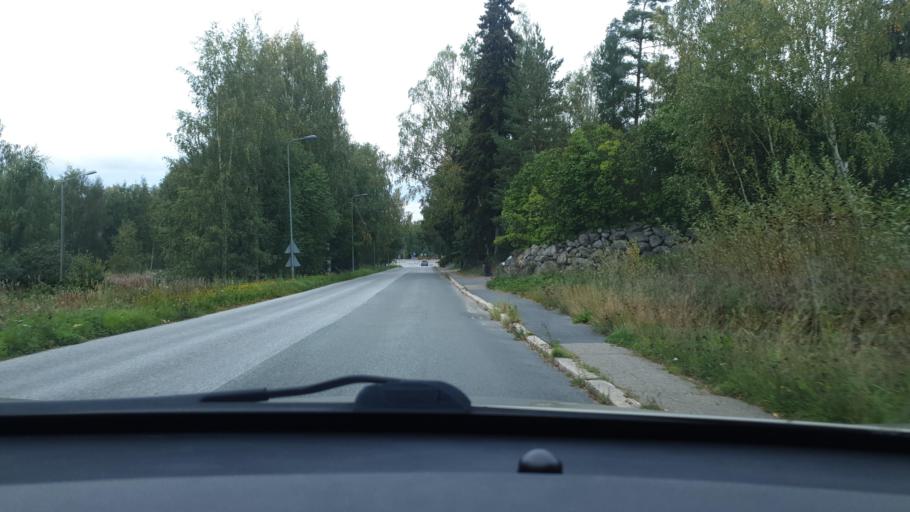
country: FI
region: Ostrobothnia
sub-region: Vaasa
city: Korsholm
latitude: 63.0969
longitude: 21.6618
